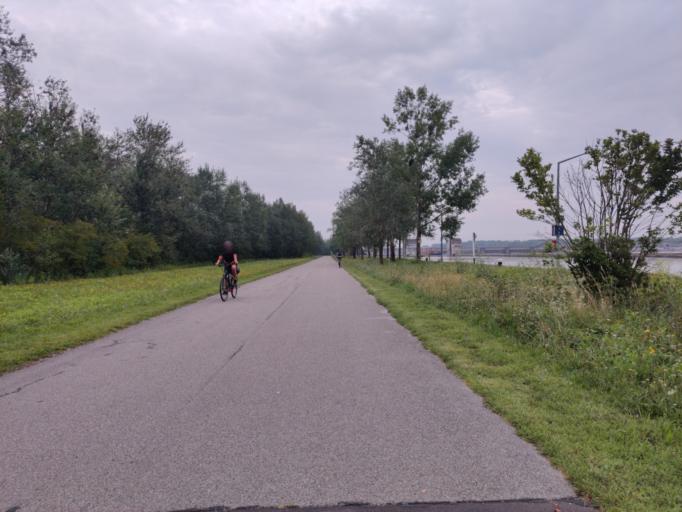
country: AT
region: Upper Austria
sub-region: Politischer Bezirk Linz-Land
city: Asten
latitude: 48.2536
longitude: 14.4256
